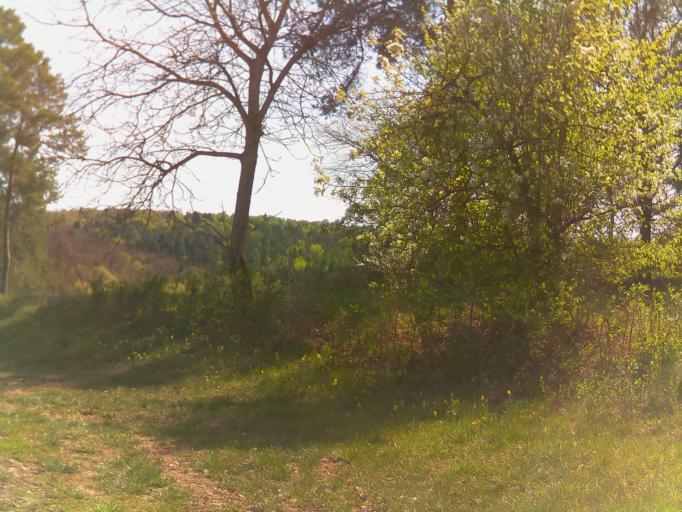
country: DE
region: Bavaria
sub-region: Regierungsbezirk Unterfranken
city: Burgpreppach
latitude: 50.1521
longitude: 10.5998
